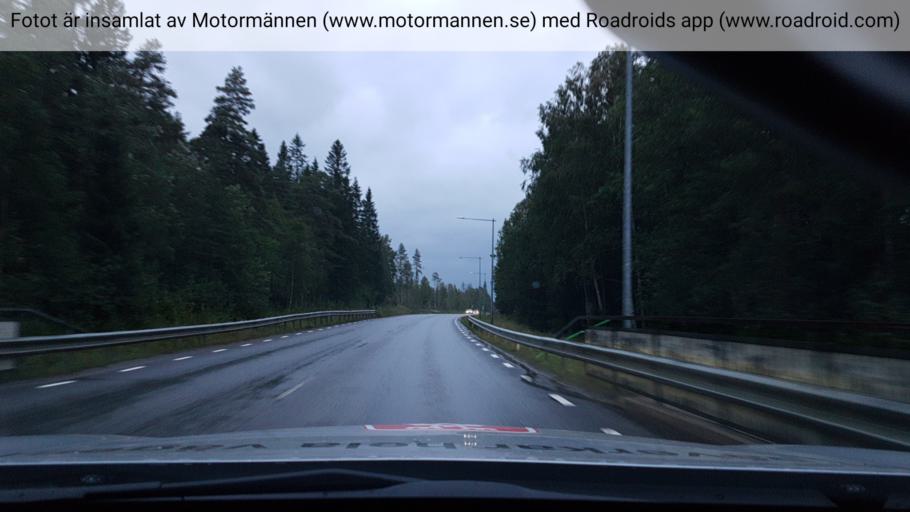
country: SE
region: Vaesterbotten
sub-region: Umea Kommun
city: Ersmark
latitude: 63.8565
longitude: 20.2979
